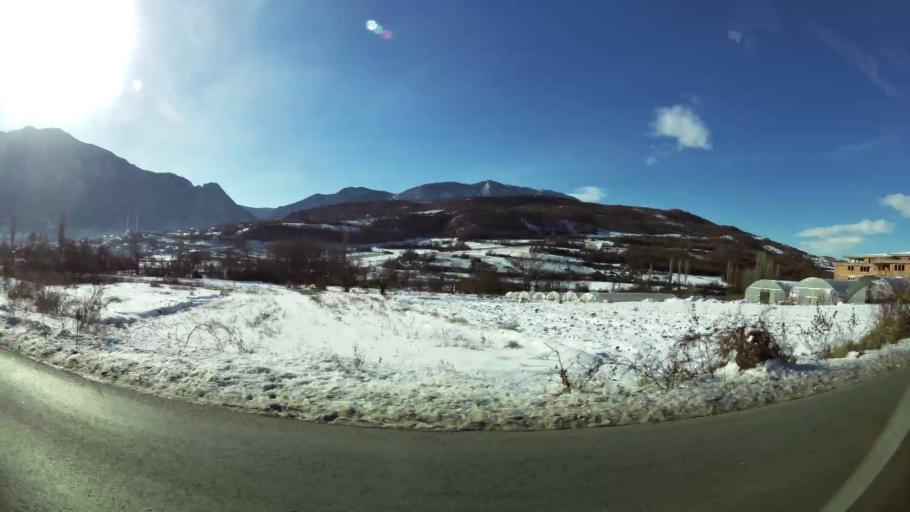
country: MK
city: Ljubin
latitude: 41.9866
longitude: 21.3006
